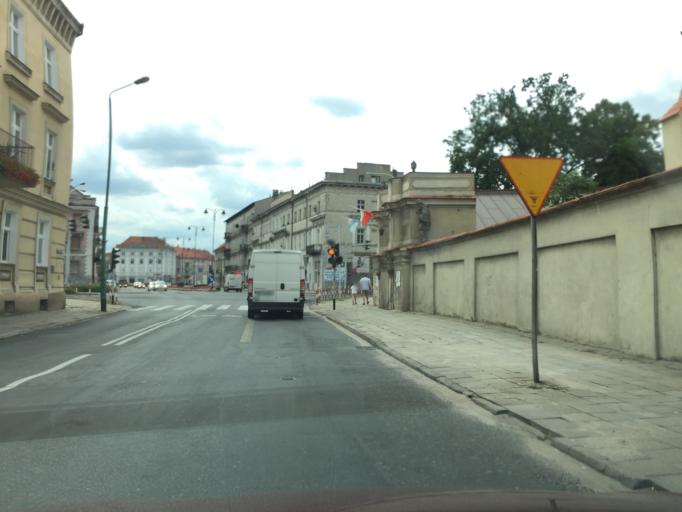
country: PL
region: Greater Poland Voivodeship
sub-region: Kalisz
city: Kalisz
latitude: 51.7665
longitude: 18.0946
